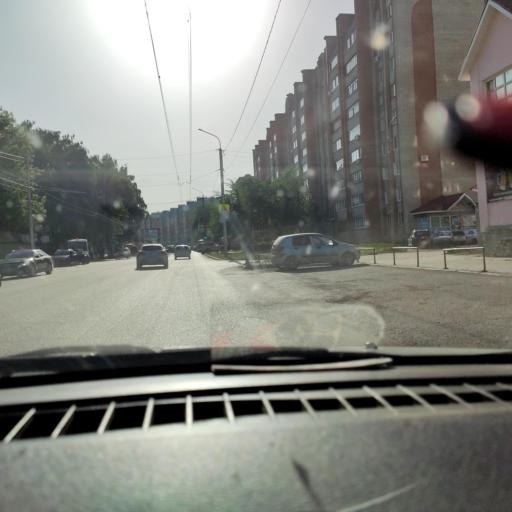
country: RU
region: Bashkortostan
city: Sterlitamak
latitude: 53.6377
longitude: 55.9046
